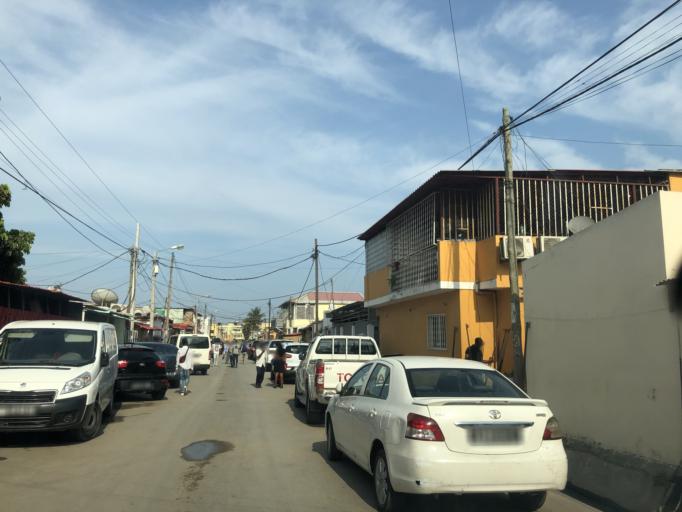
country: AO
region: Luanda
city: Luanda
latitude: -8.8290
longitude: 13.2250
